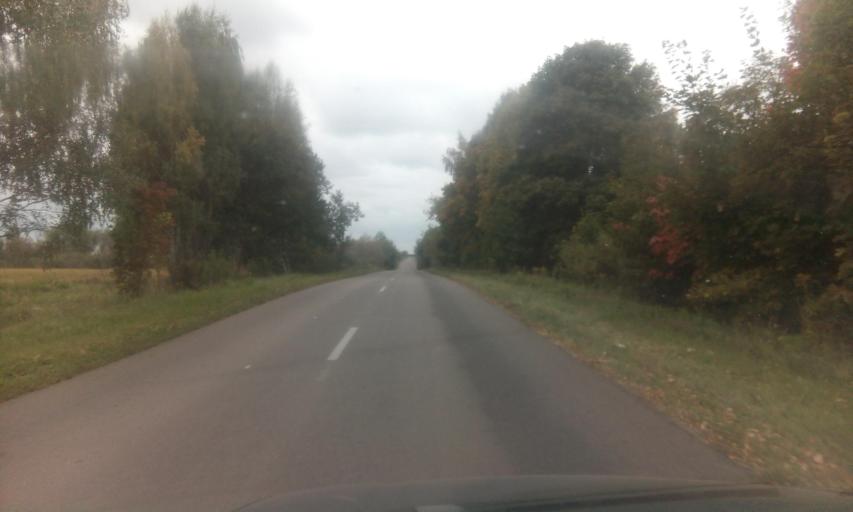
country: RU
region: Tula
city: Dubovka
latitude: 53.9605
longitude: 38.0807
